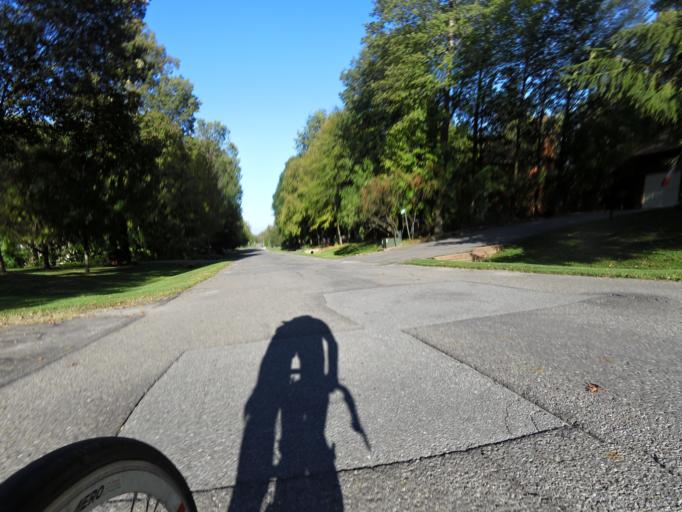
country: CA
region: Ontario
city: Bells Corners
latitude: 45.2185
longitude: -75.6903
